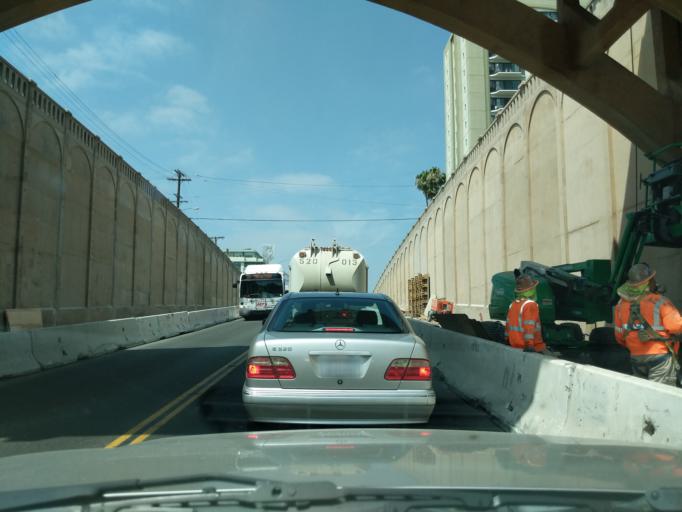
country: US
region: California
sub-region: San Diego County
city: San Diego
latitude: 32.7484
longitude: -117.1449
